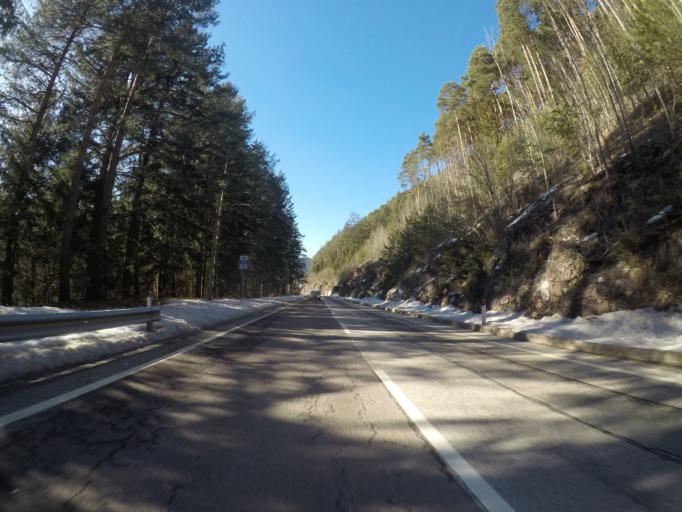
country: IT
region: Trentino-Alto Adige
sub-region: Bolzano
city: Anterivo
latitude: 46.2639
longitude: 11.3832
